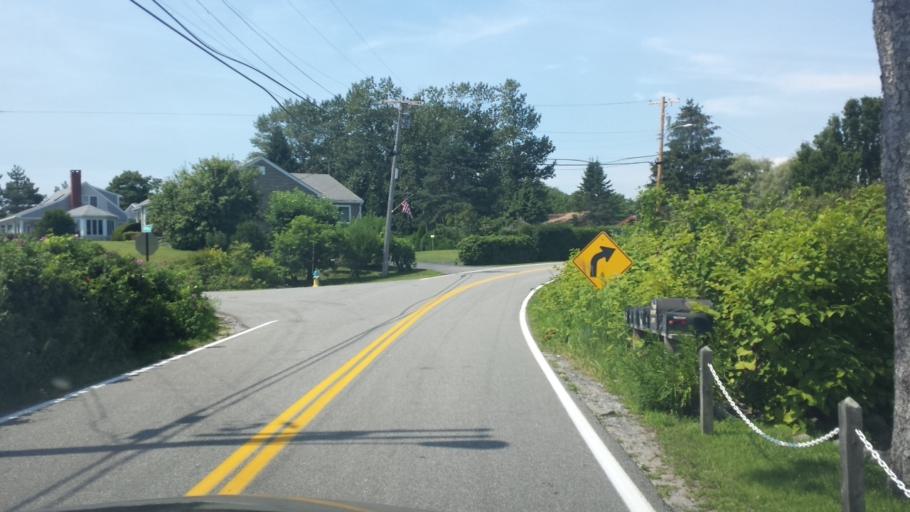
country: US
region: Maine
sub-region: York County
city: Old Orchard Beach
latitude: 43.4215
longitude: -70.3812
